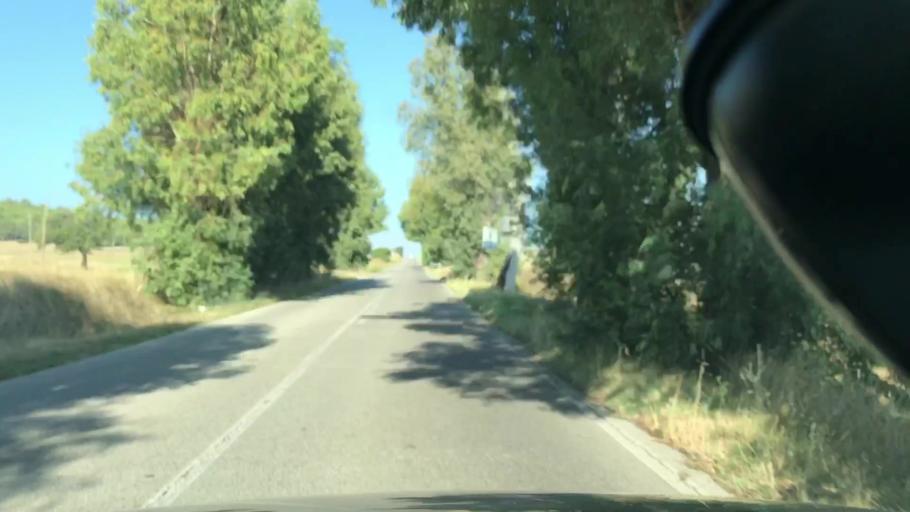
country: IT
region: Basilicate
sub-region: Provincia di Matera
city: La Martella
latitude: 40.6641
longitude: 16.4984
